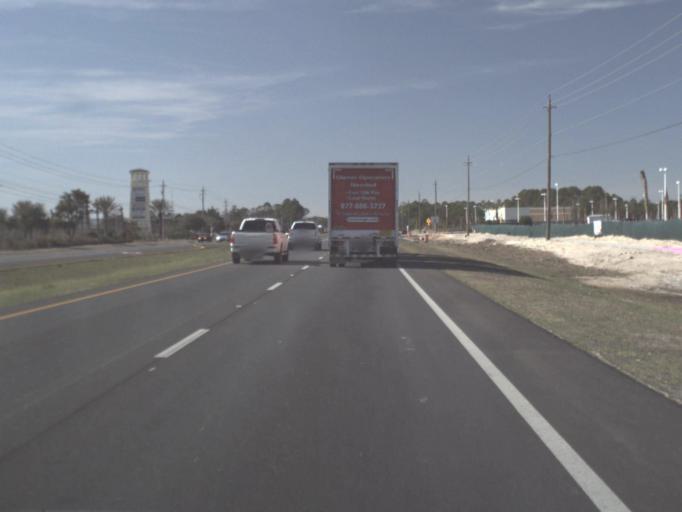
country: US
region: Florida
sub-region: Bay County
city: Laguna Beach
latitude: 30.2213
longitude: -85.8665
